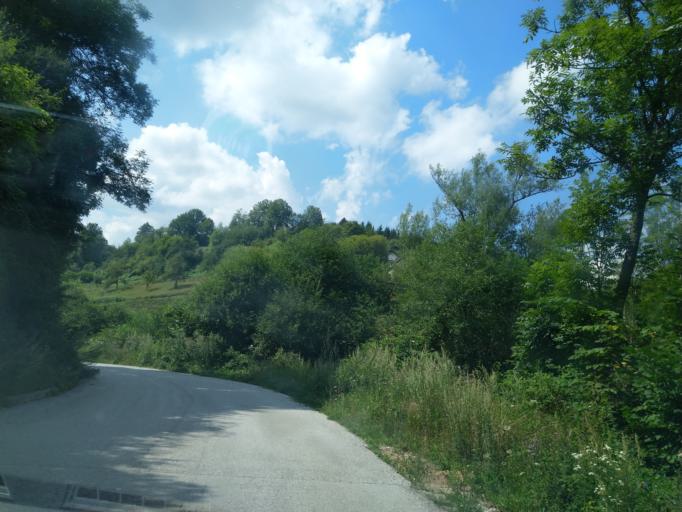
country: RS
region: Central Serbia
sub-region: Zlatiborski Okrug
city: Nova Varos
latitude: 43.5850
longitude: 19.8777
